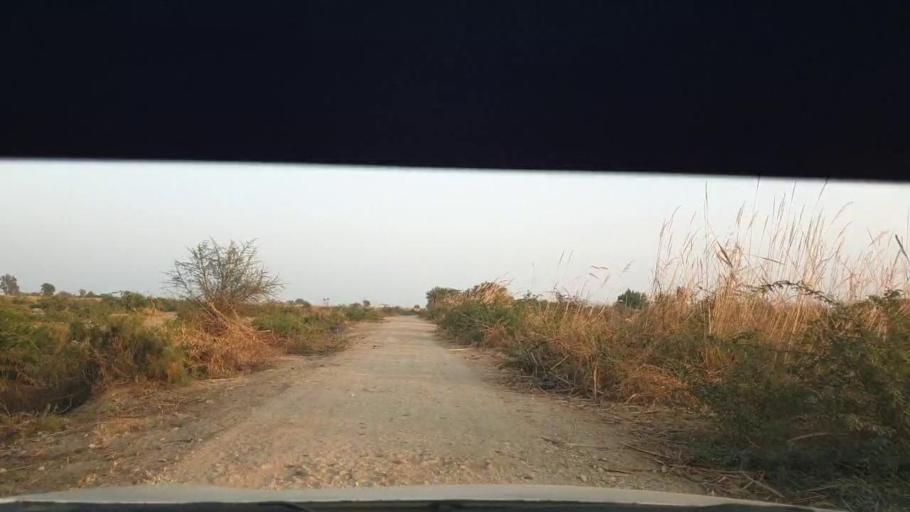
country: PK
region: Sindh
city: Berani
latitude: 25.7555
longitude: 69.0008
